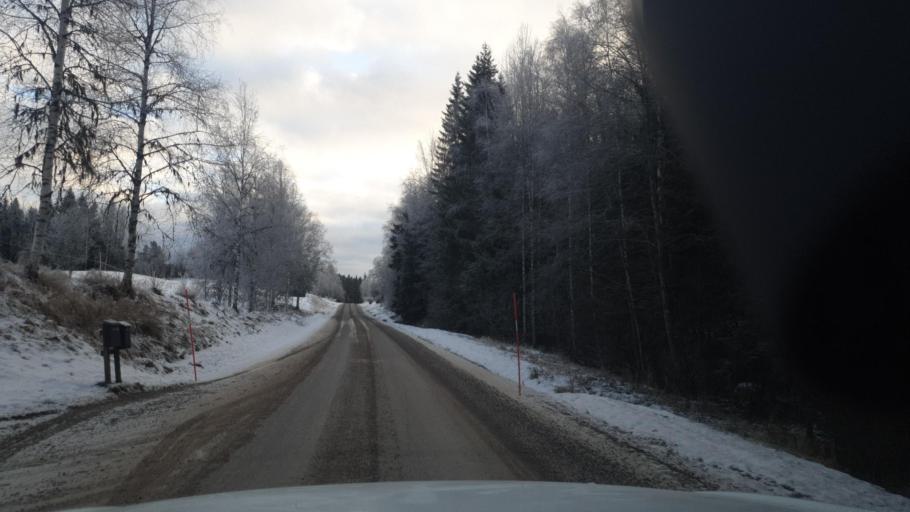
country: SE
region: Vaermland
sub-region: Eda Kommun
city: Charlottenberg
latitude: 60.0605
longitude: 12.5504
